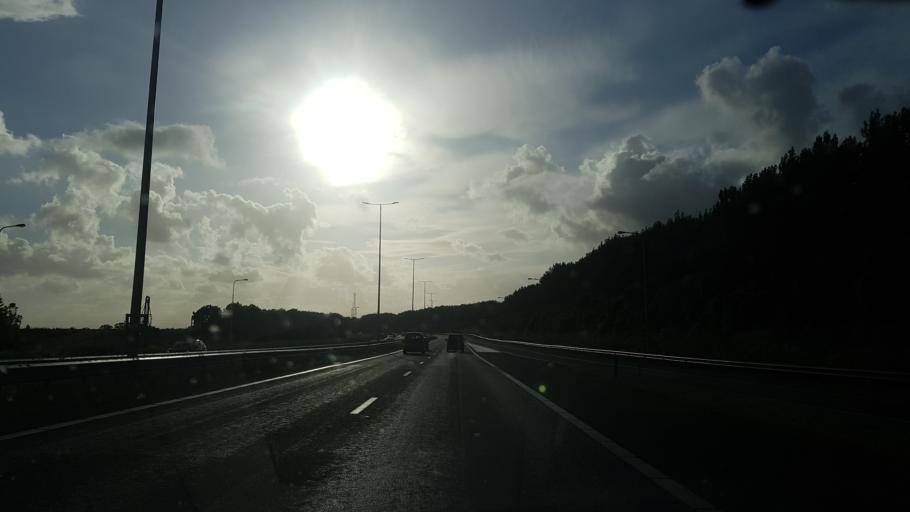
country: NL
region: Groningen
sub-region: Gemeente Groningen
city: Groningen
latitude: 53.2016
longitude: 6.5056
